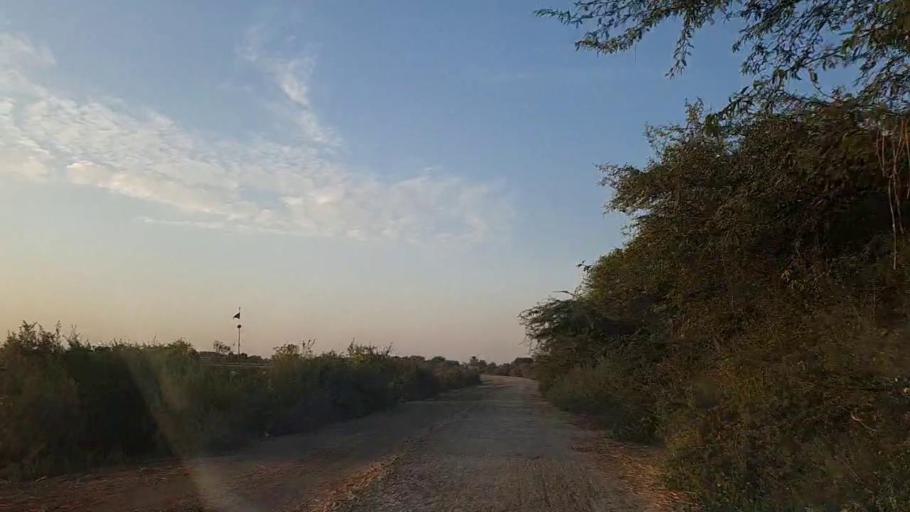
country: PK
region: Sindh
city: Chuhar Jamali
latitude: 24.4547
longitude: 68.1171
